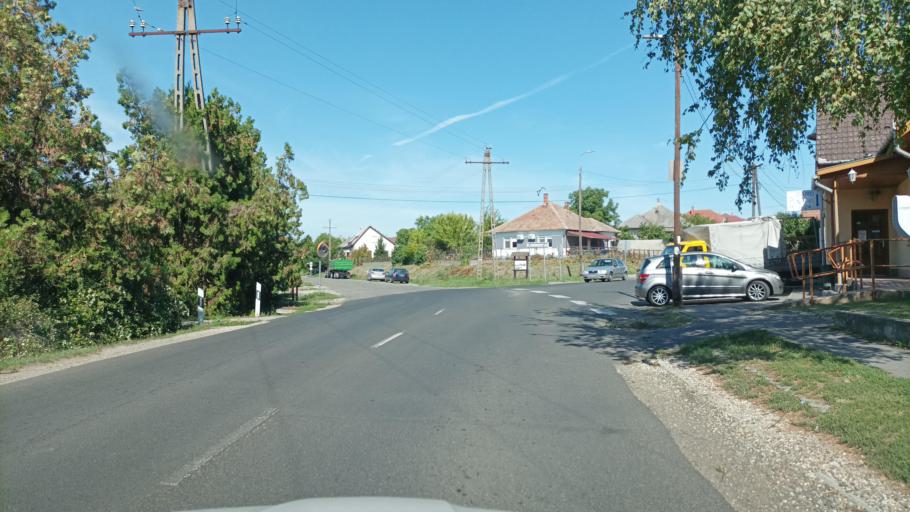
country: HU
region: Pest
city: Zsambok
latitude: 47.5456
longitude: 19.6045
